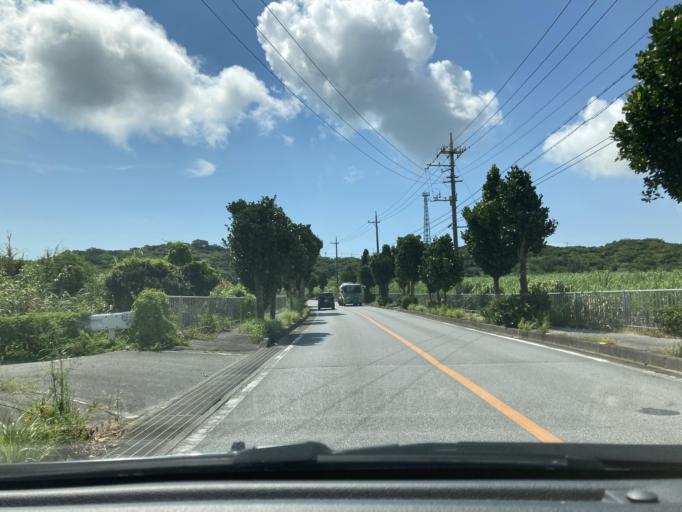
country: JP
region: Okinawa
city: Tomigusuku
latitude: 26.1555
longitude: 127.7725
